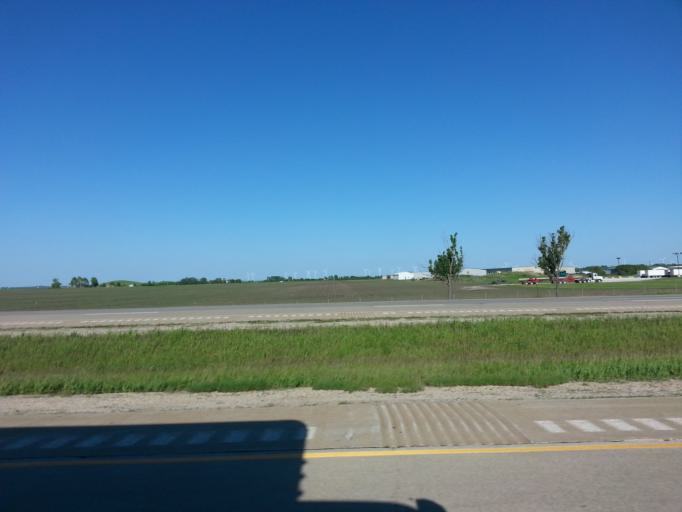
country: US
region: Illinois
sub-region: Woodford County
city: Minonk
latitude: 40.9155
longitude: -89.0568
